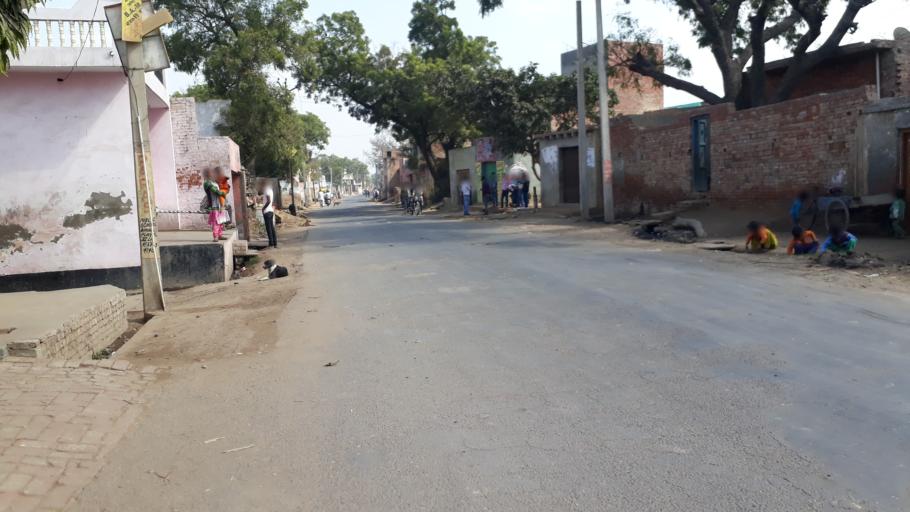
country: IN
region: Uttar Pradesh
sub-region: Baghpat
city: Baraut
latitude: 29.0956
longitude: 77.4011
